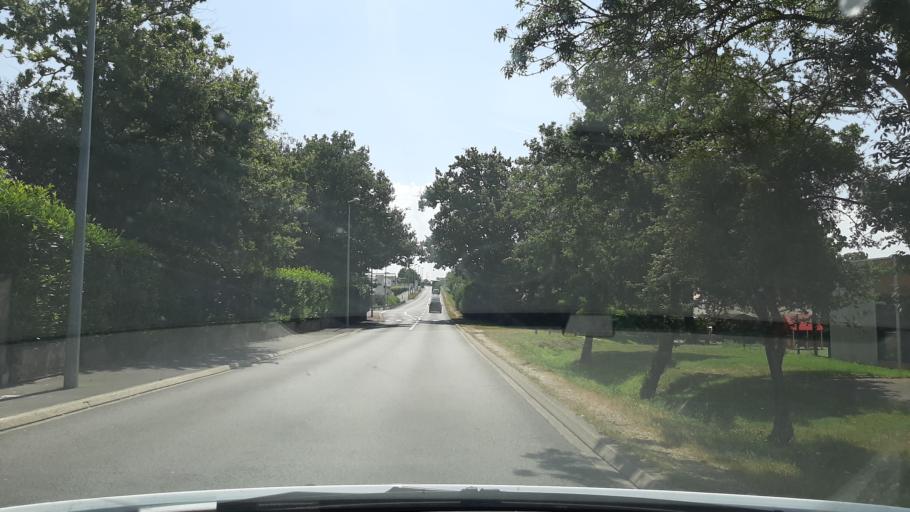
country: FR
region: Pays de la Loire
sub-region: Departement de la Vendee
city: Le Poire-sur-Vie
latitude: 46.7692
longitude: -1.5038
